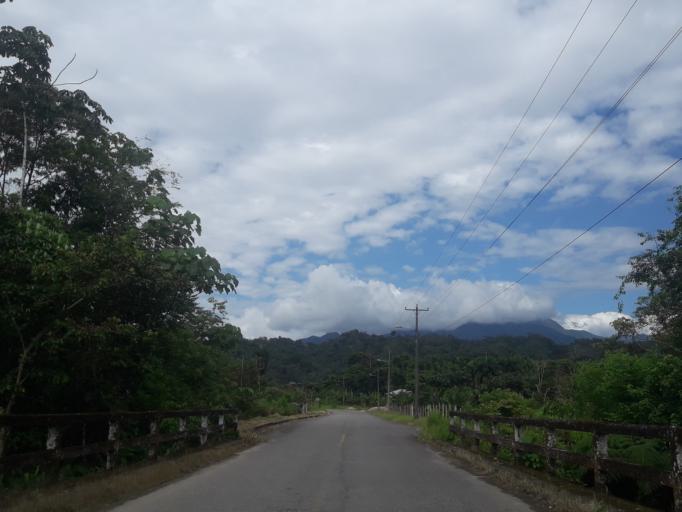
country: EC
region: Napo
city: Tena
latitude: -1.0615
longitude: -77.9030
